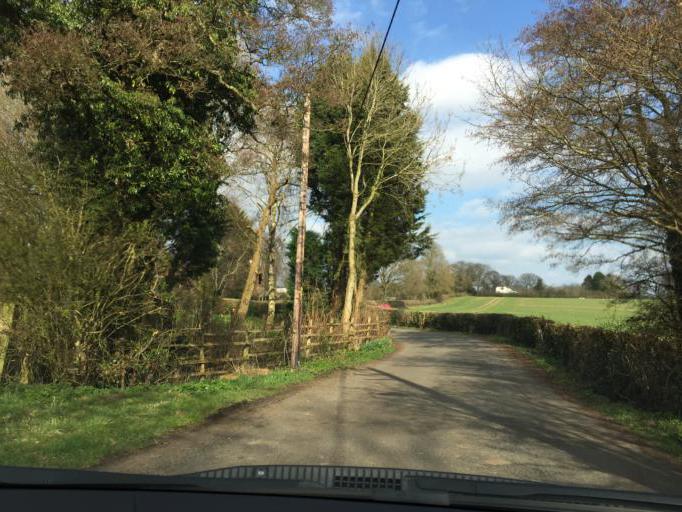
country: GB
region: England
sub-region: Solihull
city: Meriden
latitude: 52.4362
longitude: -1.5961
